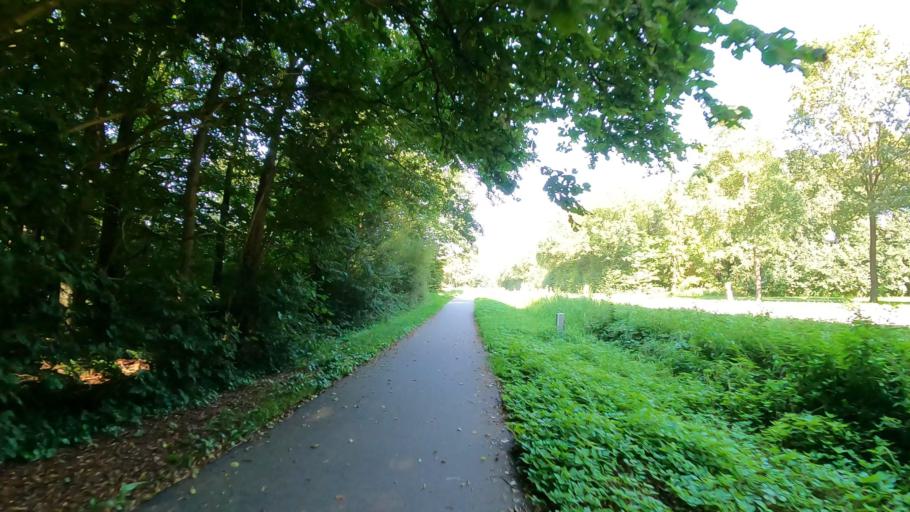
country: DE
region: Schleswig-Holstein
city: Bad Bramstedt
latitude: 53.8970
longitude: 9.8840
